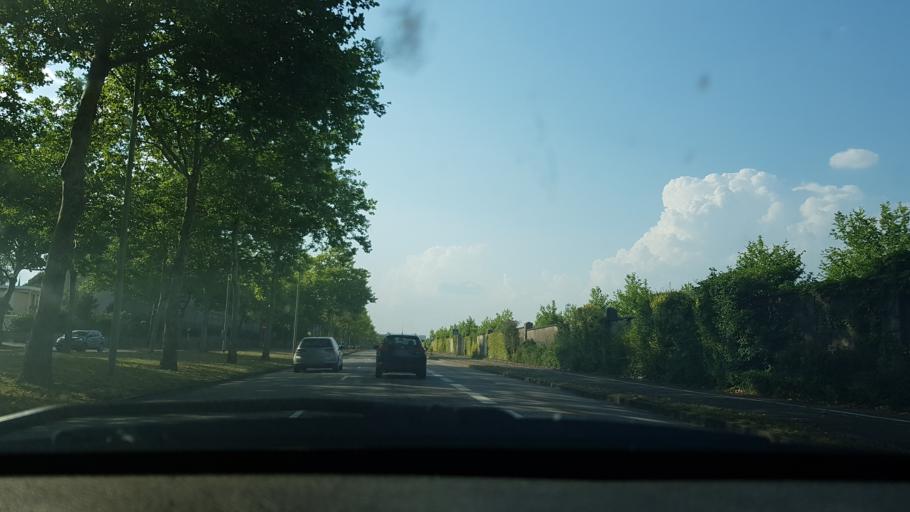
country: FR
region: Lorraine
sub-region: Departement de Meurthe-et-Moselle
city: Nancy
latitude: 48.6694
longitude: 6.1889
